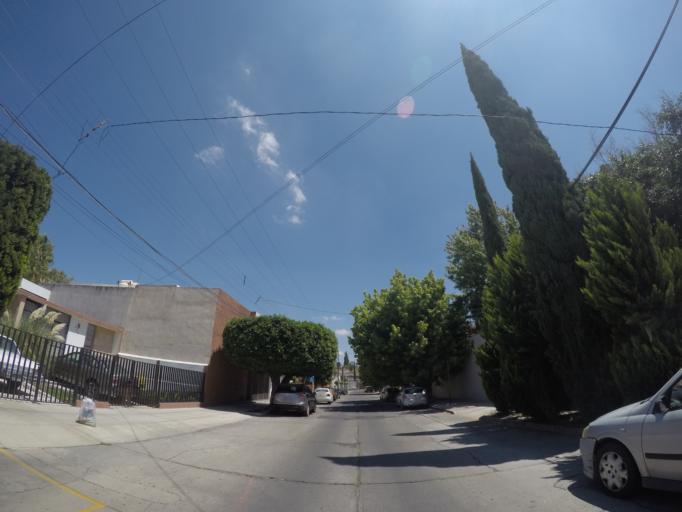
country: MX
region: San Luis Potosi
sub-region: San Luis Potosi
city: San Luis Potosi
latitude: 22.1465
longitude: -101.0068
